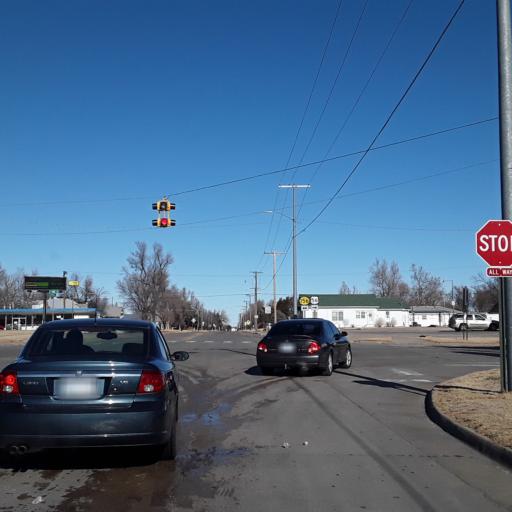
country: US
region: Kansas
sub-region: Pawnee County
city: Larned
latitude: 38.1878
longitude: -99.0984
